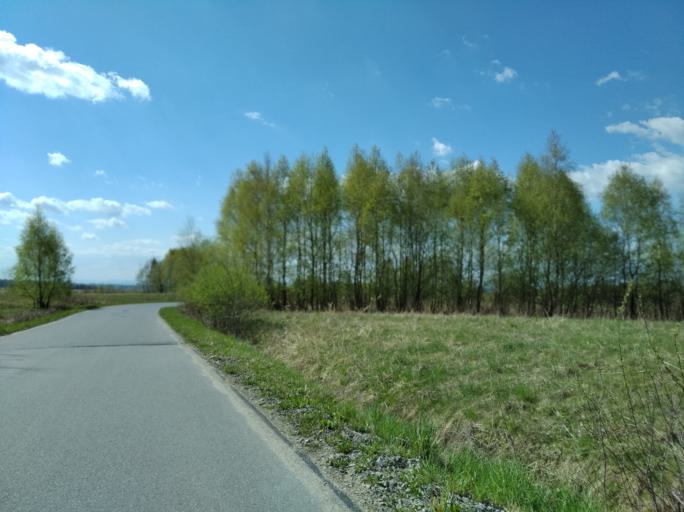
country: PL
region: Subcarpathian Voivodeship
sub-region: Powiat brzozowski
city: Golcowa
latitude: 49.8025
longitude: 22.0251
